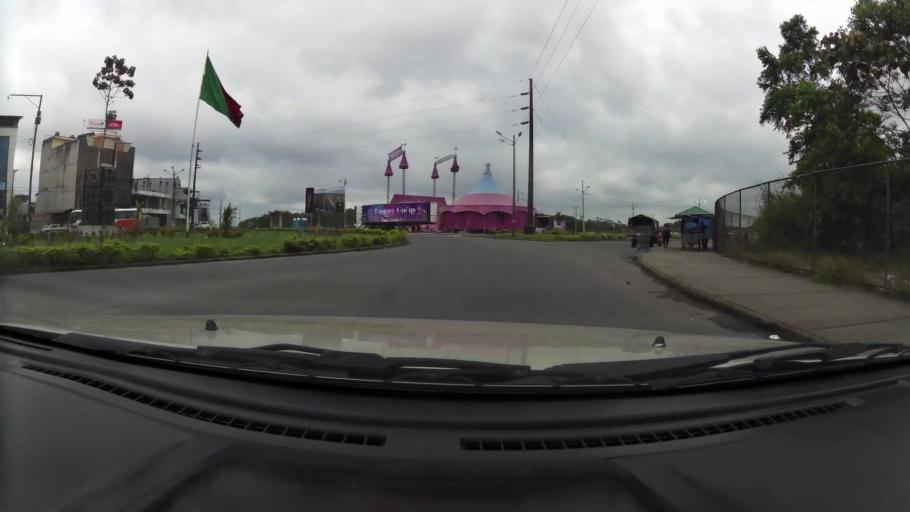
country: EC
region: Santo Domingo de los Tsachilas
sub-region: Canton Santo Domingo de los Colorados
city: Santo Domingo de los Colorados
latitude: -0.2396
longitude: -79.1631
